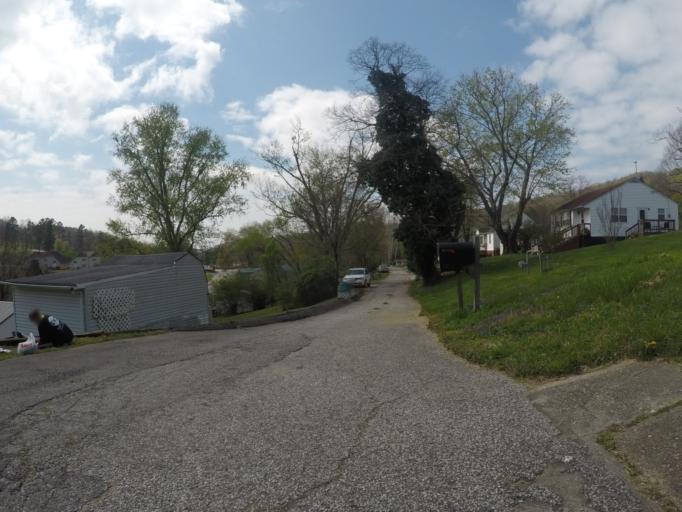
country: US
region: Ohio
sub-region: Lawrence County
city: Burlington
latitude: 38.3850
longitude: -82.5143
